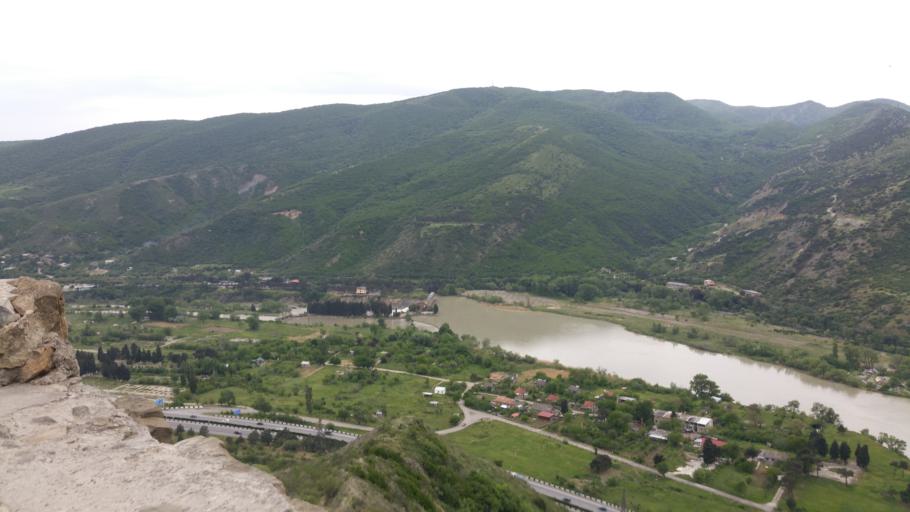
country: GE
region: Mtskheta-Mtianeti
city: Mtskheta
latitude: 41.8381
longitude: 44.7333
